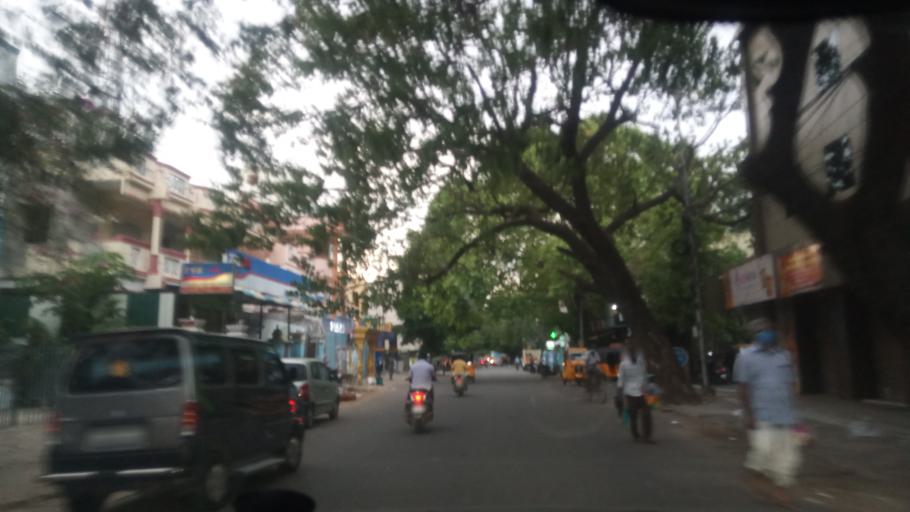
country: IN
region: Tamil Nadu
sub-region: Chennai
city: Chetput
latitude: 13.0433
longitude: 80.2222
